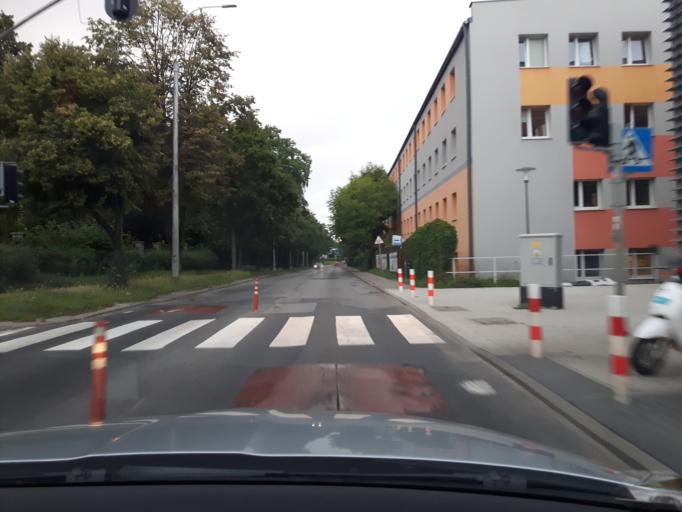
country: PL
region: Pomeranian Voivodeship
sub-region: Sopot
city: Sopot
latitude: 54.4192
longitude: 18.5604
